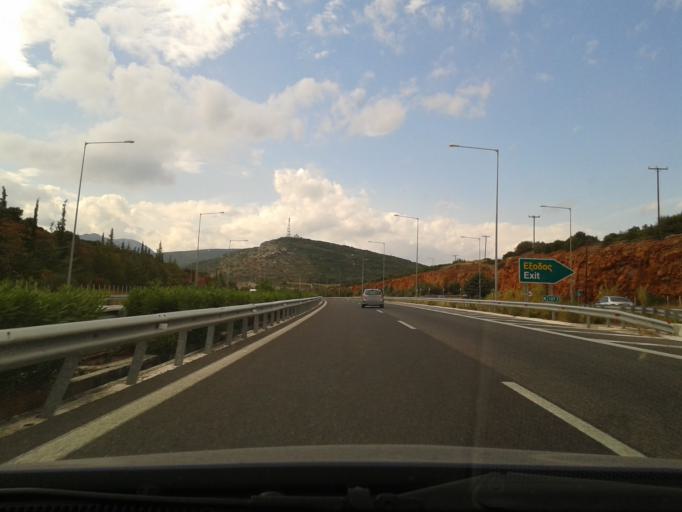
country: GR
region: Peloponnese
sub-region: Nomos Korinthias
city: Ayios Vasilios
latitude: 37.8038
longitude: 22.7358
